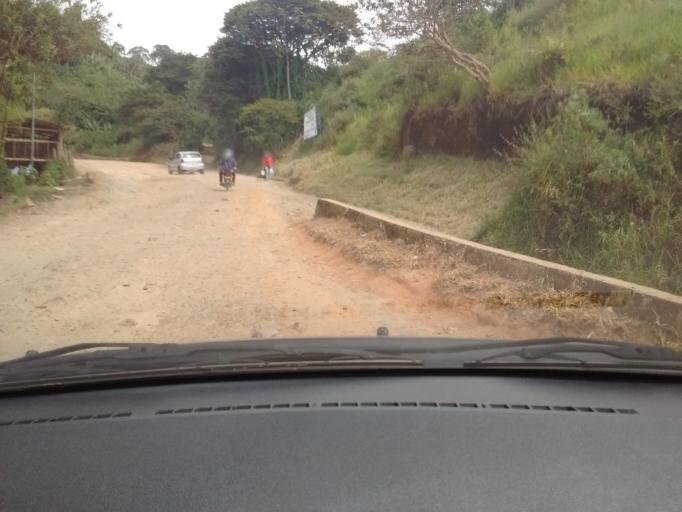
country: CO
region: Cauca
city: El Tambo
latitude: 2.4478
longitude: -76.8170
